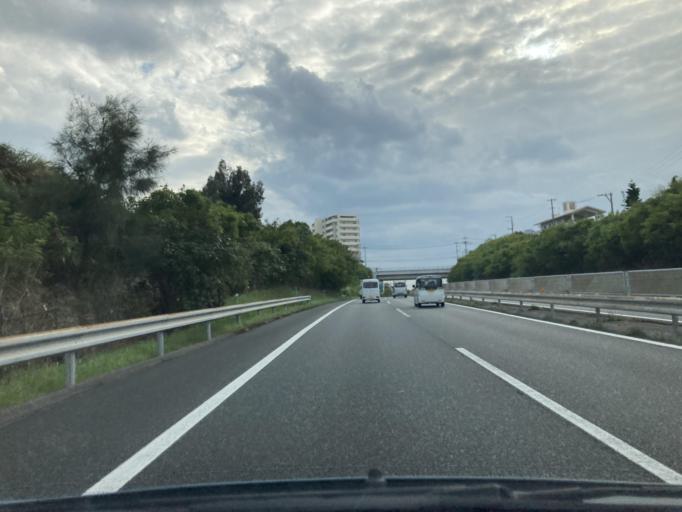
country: JP
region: Okinawa
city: Ginowan
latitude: 26.2598
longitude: 127.7700
